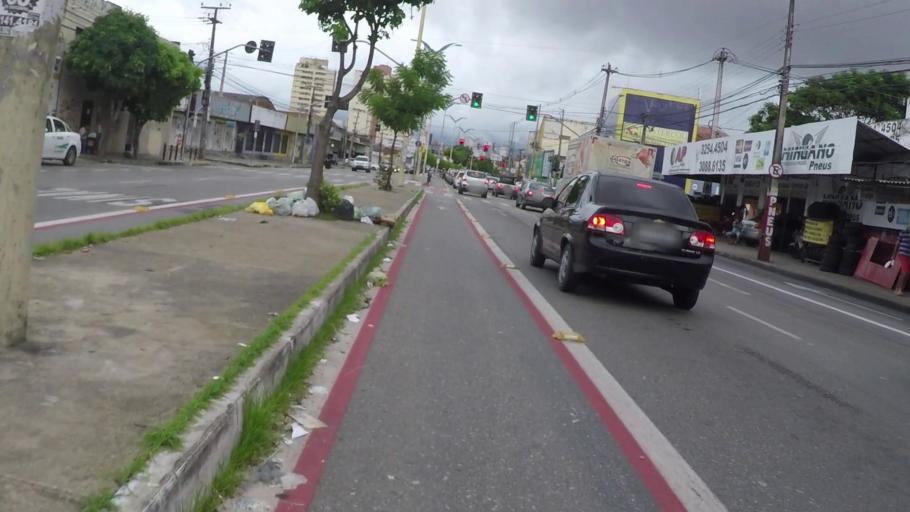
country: BR
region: Ceara
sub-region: Fortaleza
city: Fortaleza
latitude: -3.7369
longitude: -38.5295
